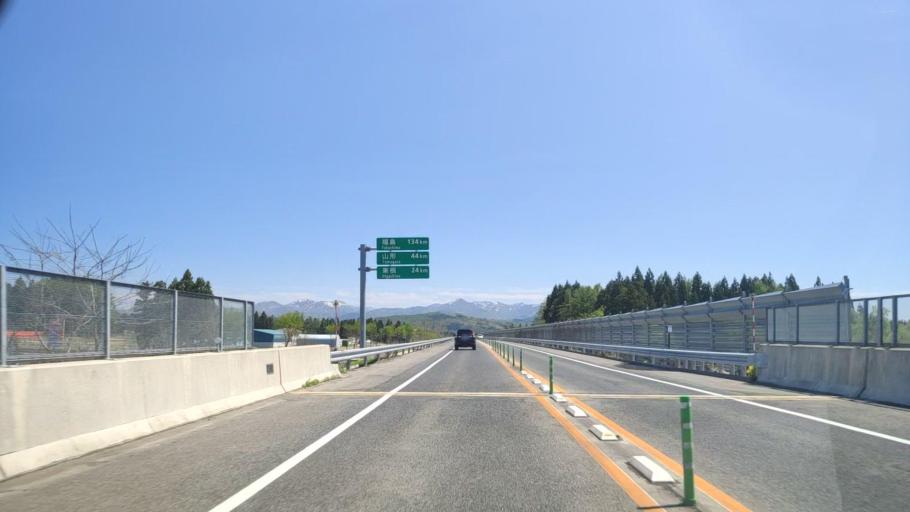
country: JP
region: Yamagata
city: Obanazawa
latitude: 38.6217
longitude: 140.3808
